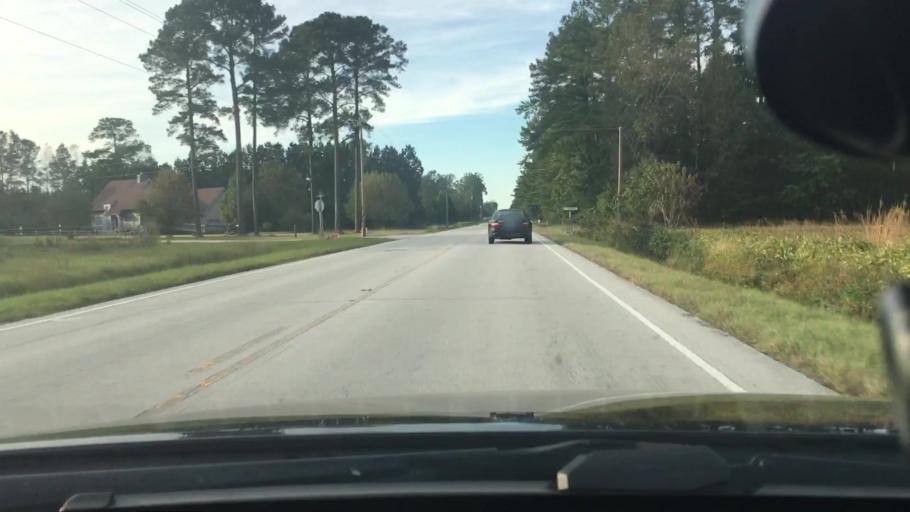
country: US
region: North Carolina
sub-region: Craven County
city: Vanceboro
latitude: 35.3583
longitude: -77.1950
